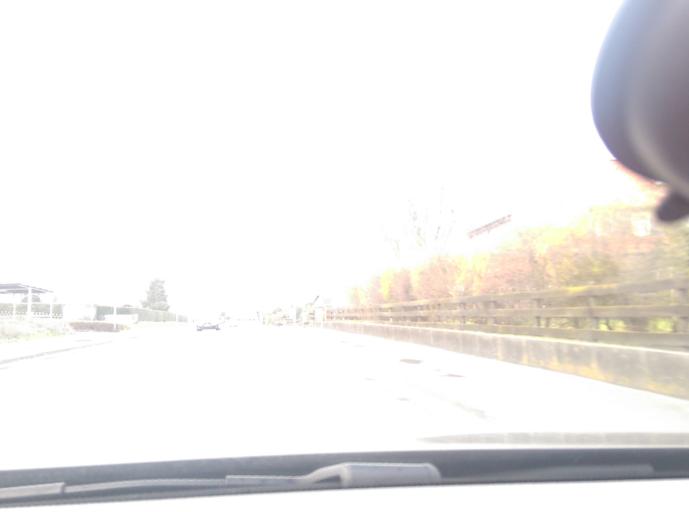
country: DE
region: Lower Saxony
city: Schwarmstedt
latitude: 52.5818
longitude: 9.5888
